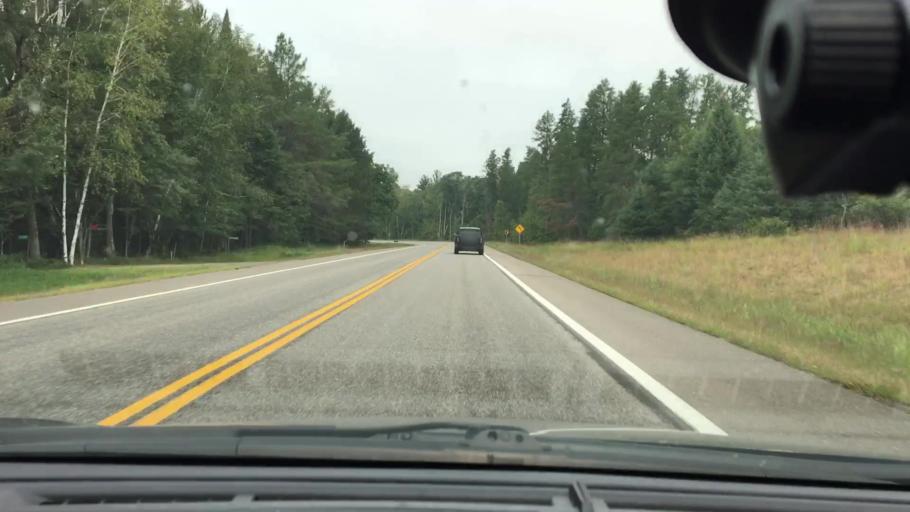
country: US
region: Minnesota
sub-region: Crow Wing County
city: Cross Lake
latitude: 46.6643
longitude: -94.0380
